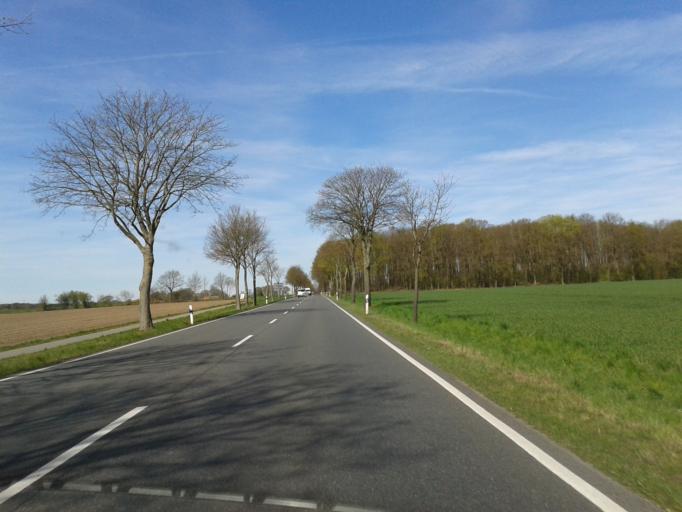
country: DE
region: Lower Saxony
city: Suhlendorf
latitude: 52.9333
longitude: 10.7660
